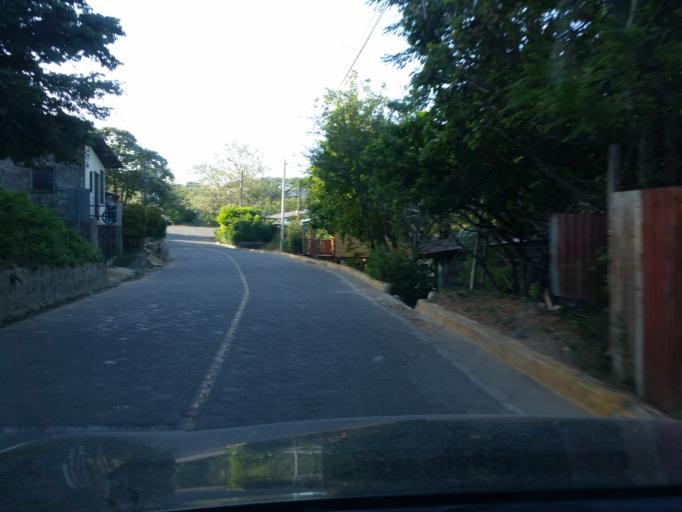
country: NI
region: Rivas
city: San Juan del Sur
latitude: 11.2568
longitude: -85.8640
